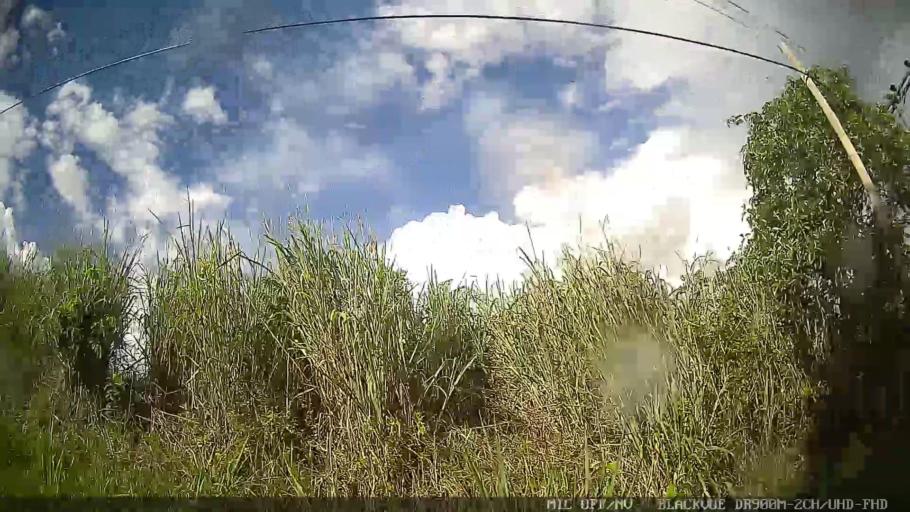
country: BR
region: Sao Paulo
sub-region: Jaguariuna
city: Jaguariuna
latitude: -22.6638
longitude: -47.0365
